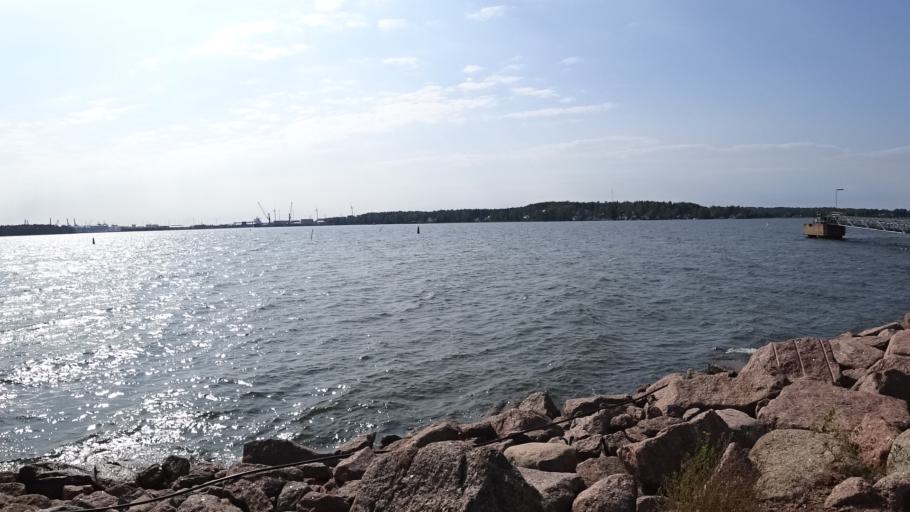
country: FI
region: Kymenlaakso
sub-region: Kotka-Hamina
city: Kotka
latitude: 60.4475
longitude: 26.9356
